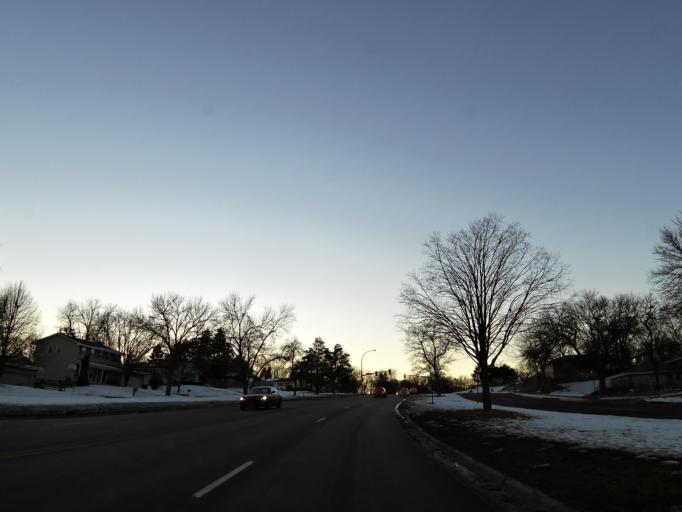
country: US
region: Minnesota
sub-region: Hennepin County
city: Bloomington
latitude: 44.8253
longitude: -93.3361
